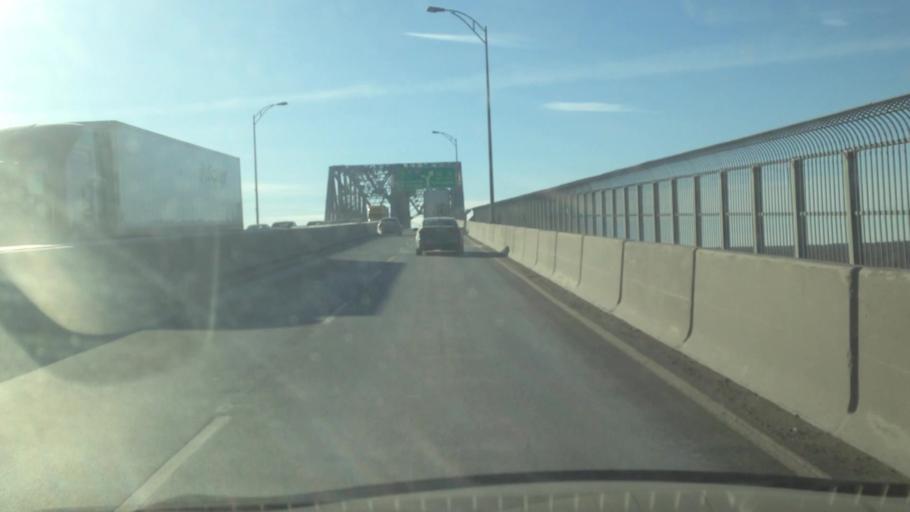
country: CA
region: Quebec
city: Montreal-Ouest
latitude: 45.4113
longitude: -73.6580
